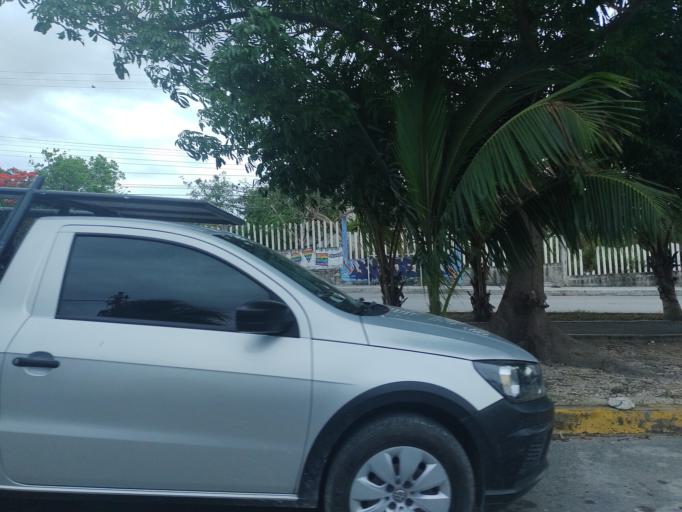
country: MX
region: Quintana Roo
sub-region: Tulum
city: Ciudad Chemuyil
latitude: 20.4006
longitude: -87.3216
